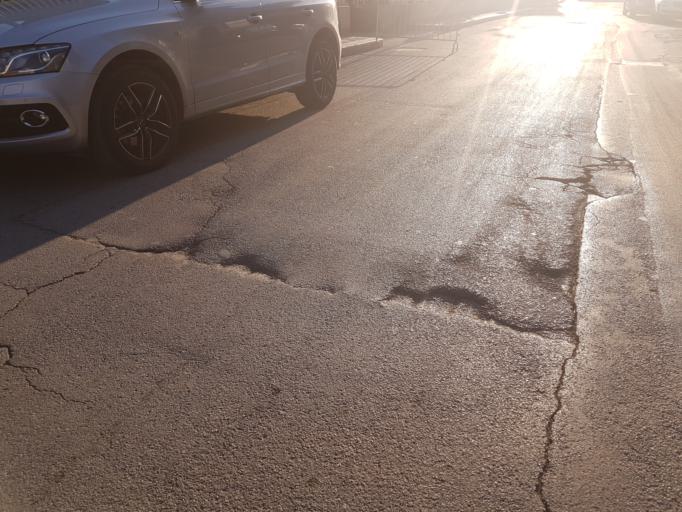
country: IT
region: Apulia
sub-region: Provincia di Bari
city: Corato
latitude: 41.1457
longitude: 16.4134
